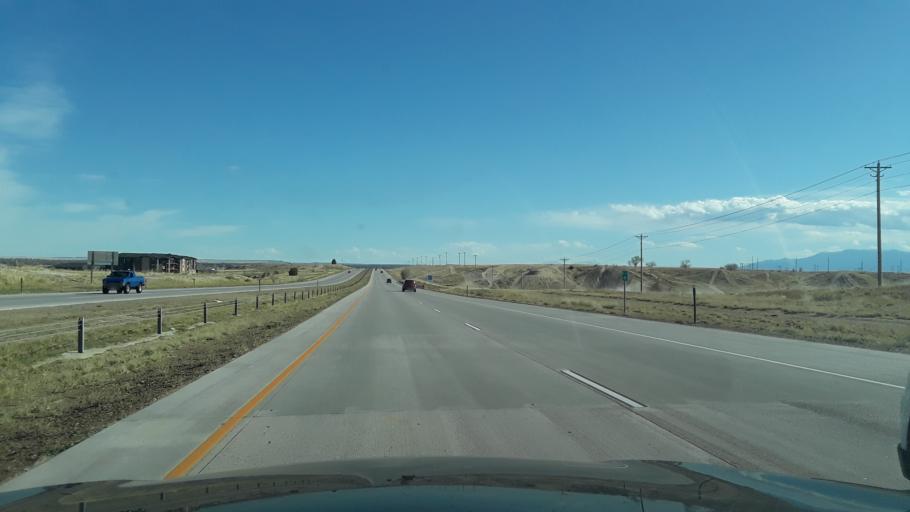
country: US
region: Colorado
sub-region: Pueblo County
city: Pueblo West
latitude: 38.3061
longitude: -104.6638
